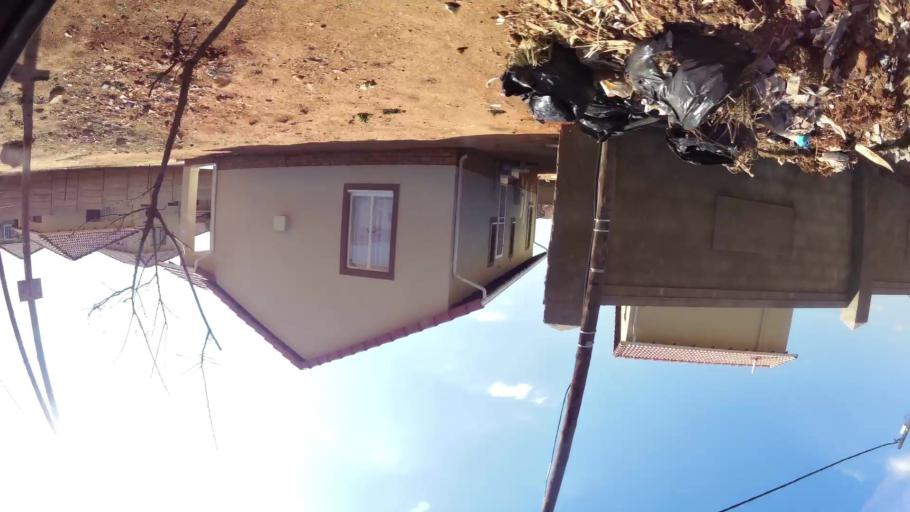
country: ZA
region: Gauteng
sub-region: West Rand District Municipality
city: Muldersdriseloop
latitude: -26.0280
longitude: 27.9389
